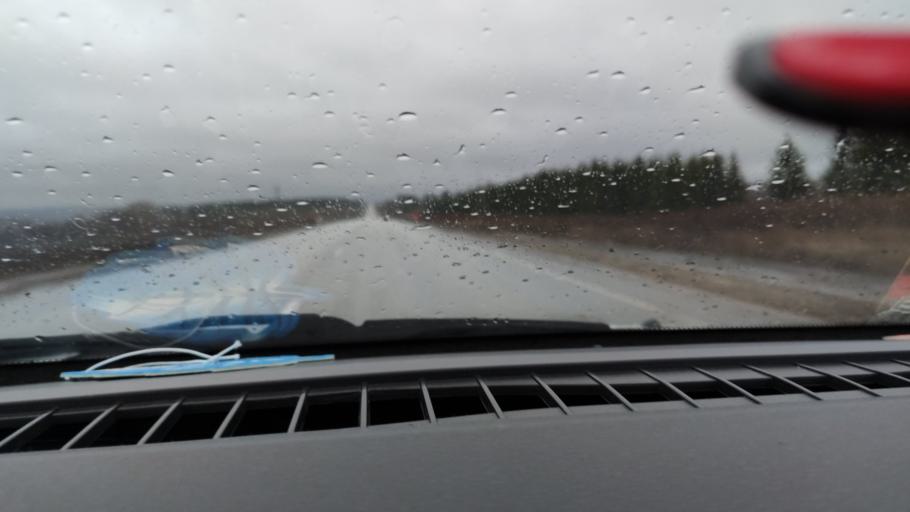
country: RU
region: Udmurtiya
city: Alnashi
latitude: 56.0616
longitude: 52.3945
